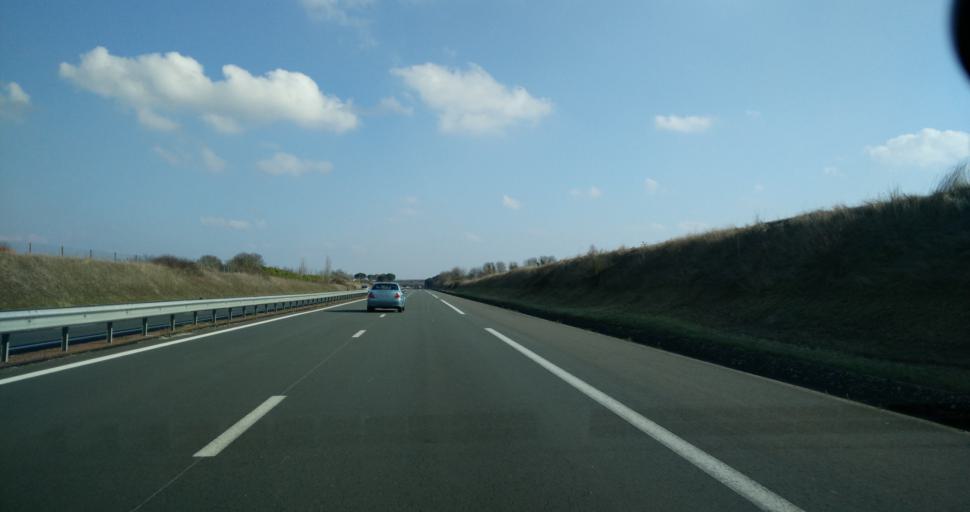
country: FR
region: Poitou-Charentes
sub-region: Departement de la Charente-Maritime
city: Saint-Jean-de-Liversay
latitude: 46.2258
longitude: -0.8695
